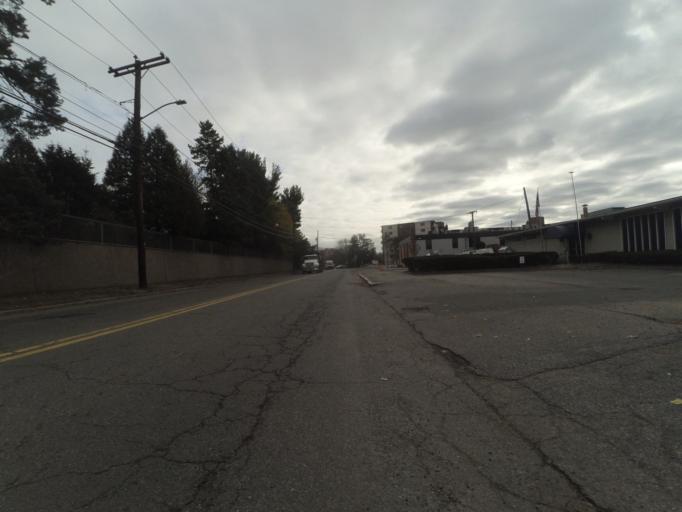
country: US
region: Massachusetts
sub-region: Middlesex County
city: Watertown
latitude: 42.3665
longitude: -71.1480
